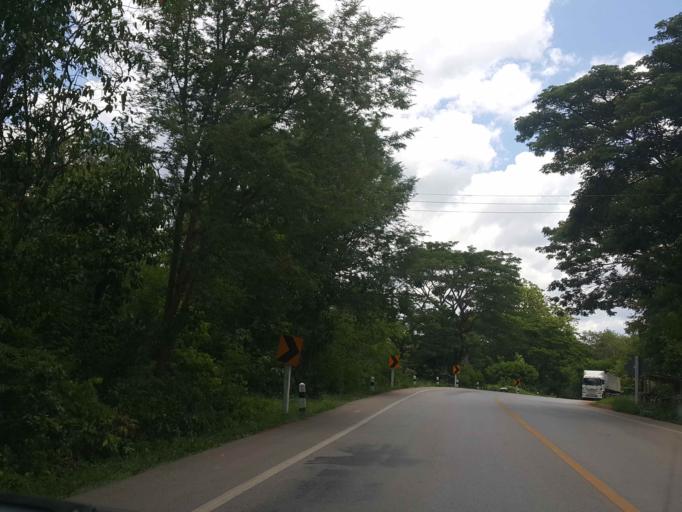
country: TH
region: Nan
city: Wiang Sa
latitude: 18.5174
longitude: 100.5920
